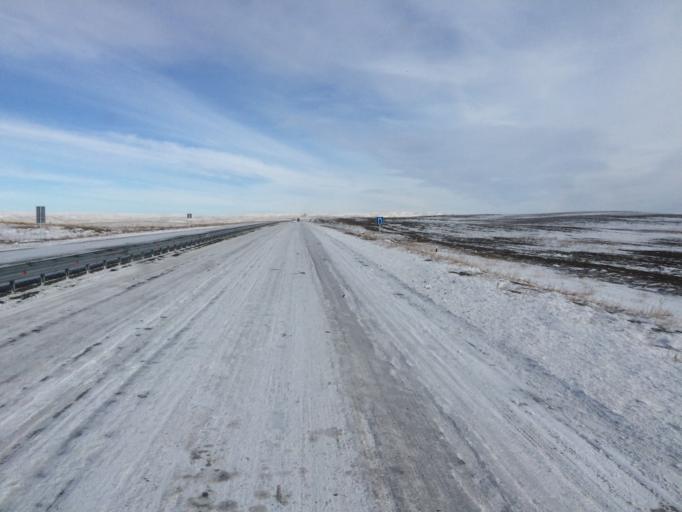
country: KZ
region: Zhambyl
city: Georgiyevka
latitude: 43.3690
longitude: 74.7307
